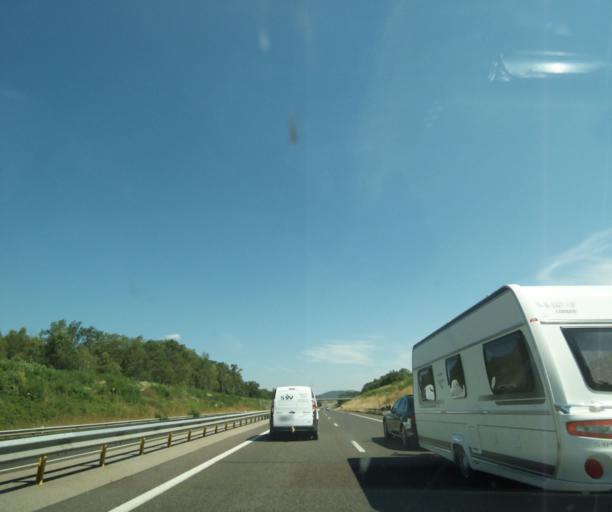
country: FR
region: Lorraine
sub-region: Departement de Meurthe-et-Moselle
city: Dommartin-les-Toul
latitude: 48.6400
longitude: 5.8806
